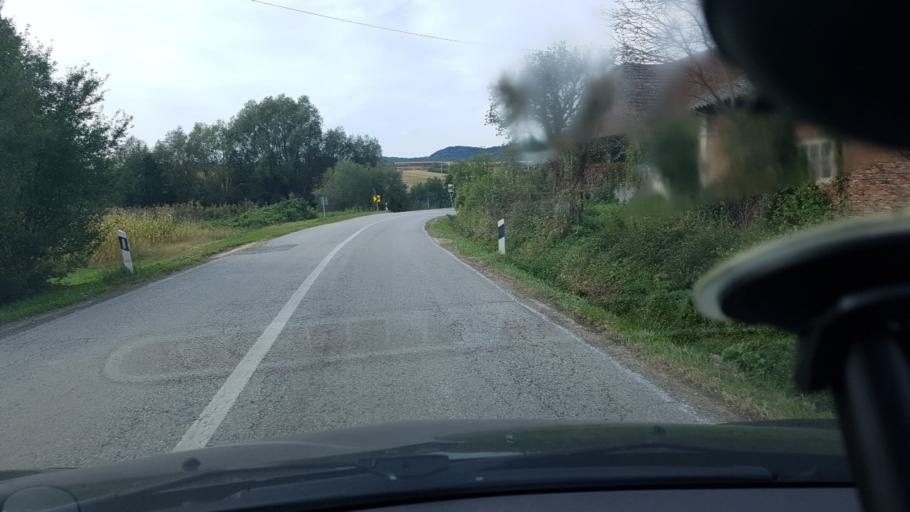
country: HR
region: Varazdinska
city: Ljubescica
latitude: 46.1036
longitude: 16.3941
